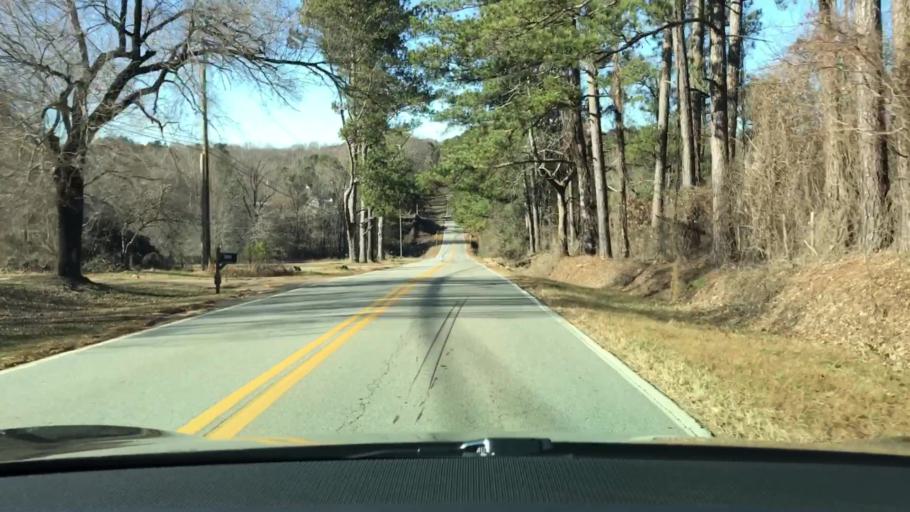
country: US
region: Georgia
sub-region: Barrow County
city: Auburn
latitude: 34.0476
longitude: -83.8459
